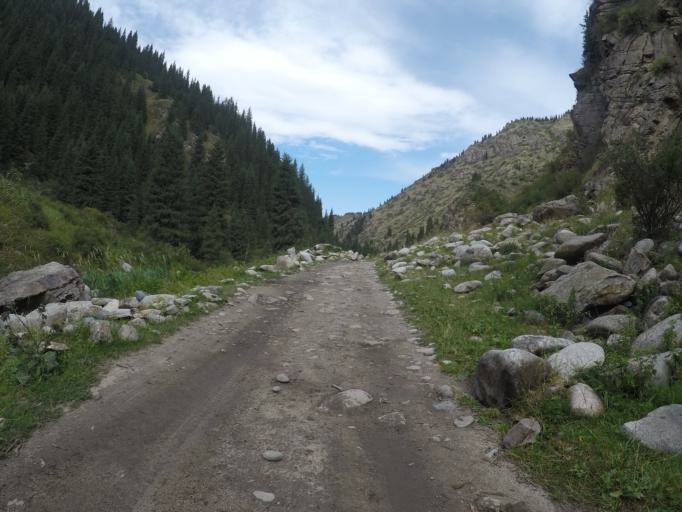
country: KG
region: Ysyk-Koel
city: Teploklyuchenka
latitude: 42.4385
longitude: 78.5592
